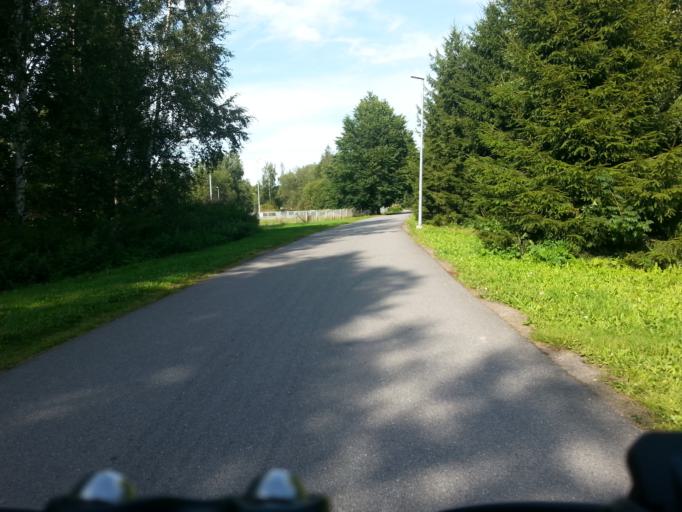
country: FI
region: Uusimaa
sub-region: Helsinki
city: Vantaa
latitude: 60.2380
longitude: 24.9941
